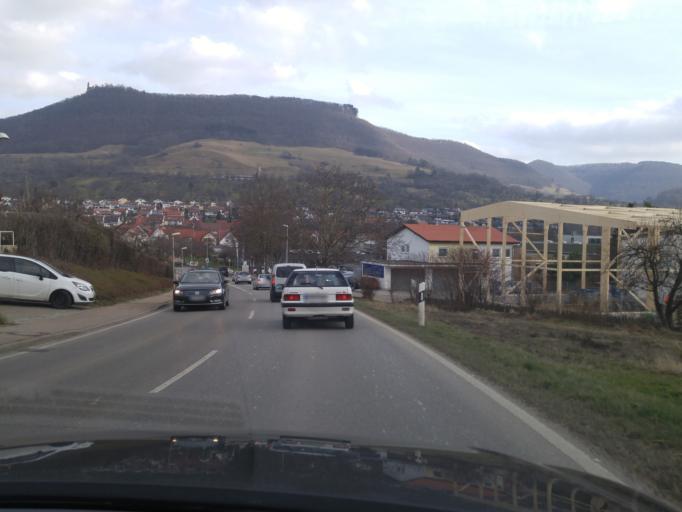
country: DE
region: Baden-Wuerttemberg
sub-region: Regierungsbezirk Stuttgart
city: Owen
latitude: 48.5841
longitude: 9.4435
